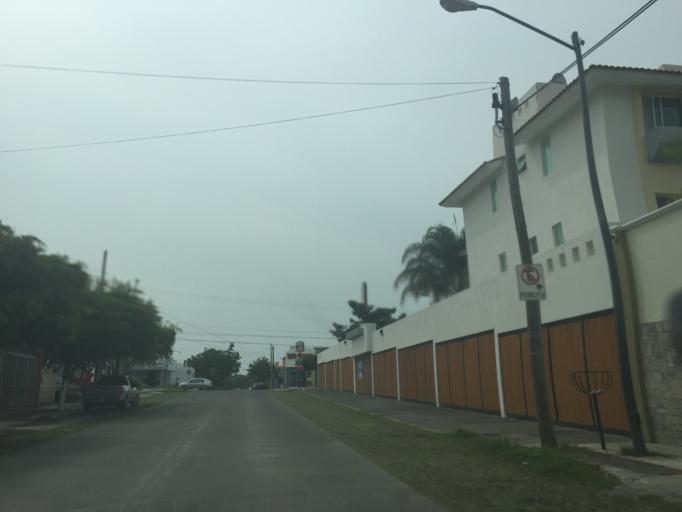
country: MX
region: Colima
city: Colima
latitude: 19.2613
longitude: -103.7137
